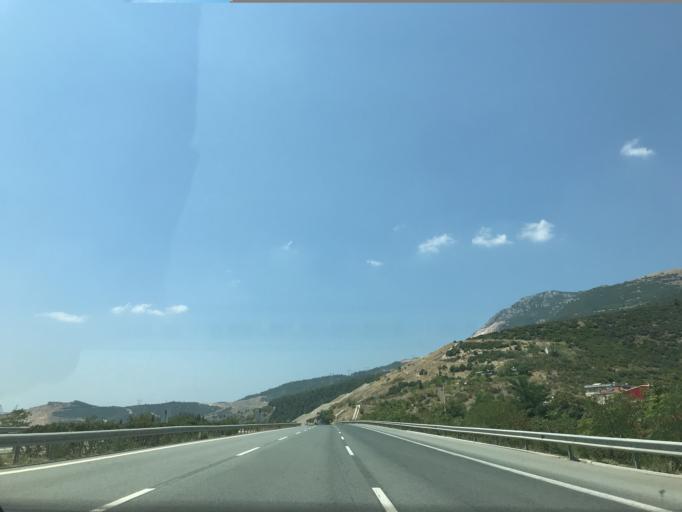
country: TR
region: Bursa
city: Gursu
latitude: 40.2471
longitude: 29.2469
